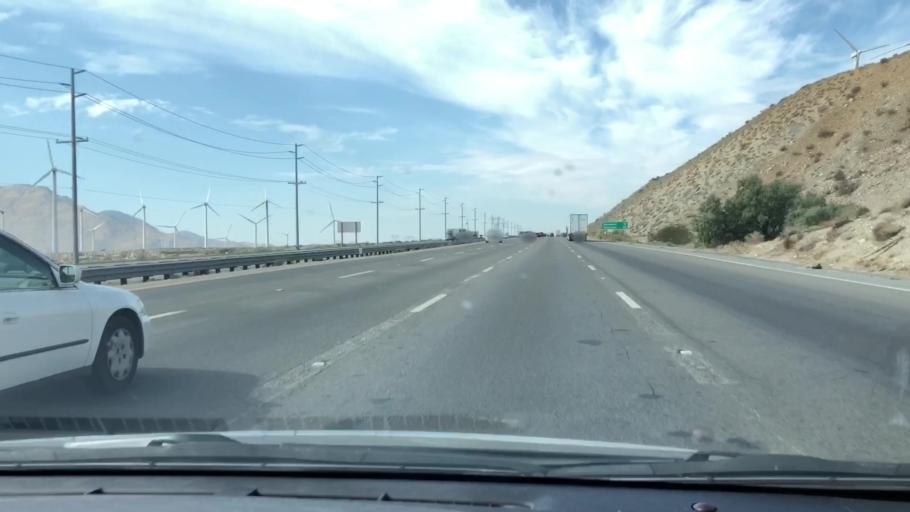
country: US
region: California
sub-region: Riverside County
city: Garnet
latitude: 33.9174
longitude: -116.6175
